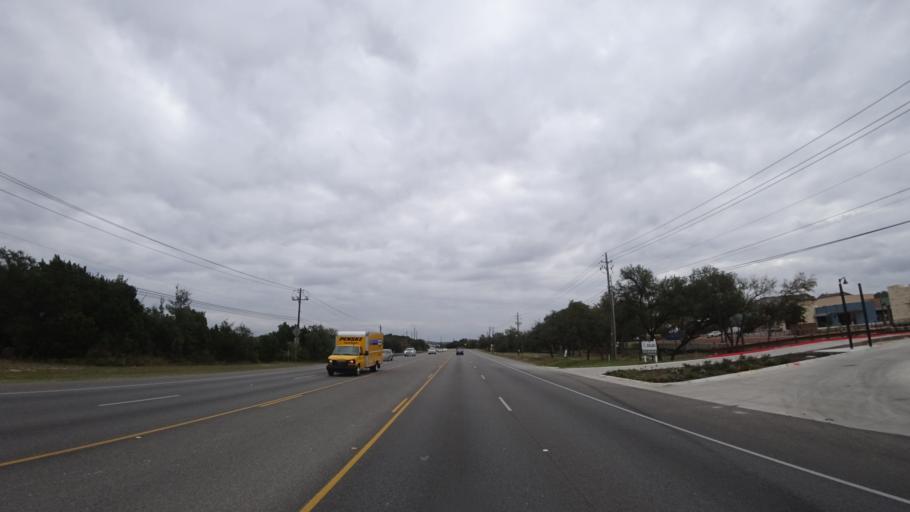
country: US
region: Texas
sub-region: Travis County
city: Bee Cave
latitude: 30.3238
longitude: -97.9570
